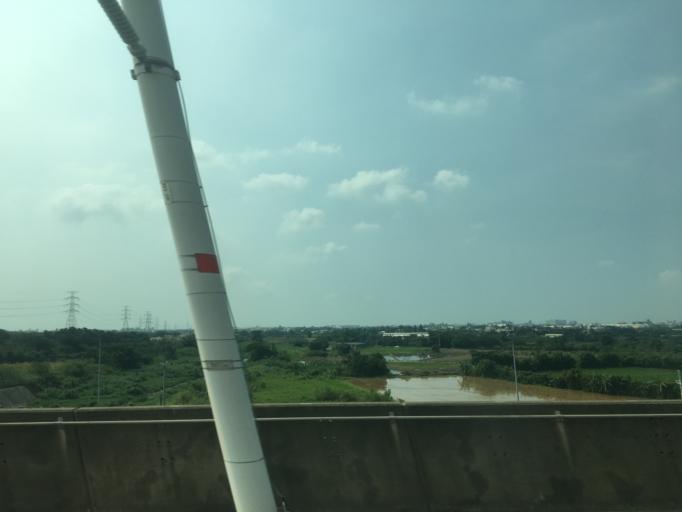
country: TW
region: Taiwan
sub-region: Hsinchu
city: Zhubei
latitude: 24.9406
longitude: 121.1164
